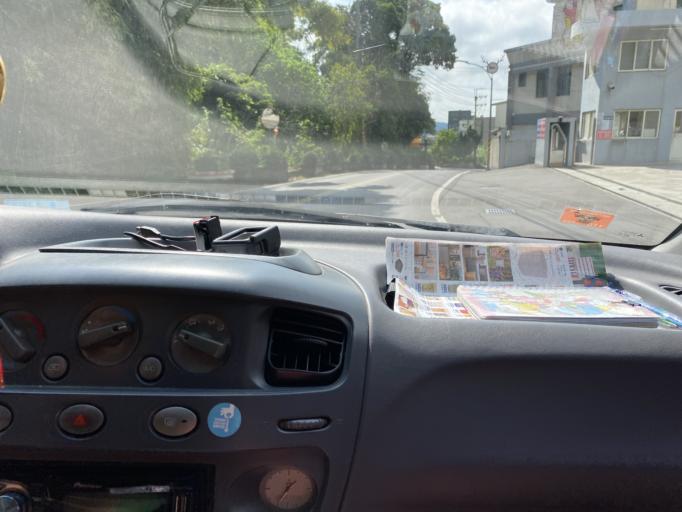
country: TW
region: Taiwan
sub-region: Hsinchu
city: Zhubei
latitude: 24.7389
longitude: 121.1319
